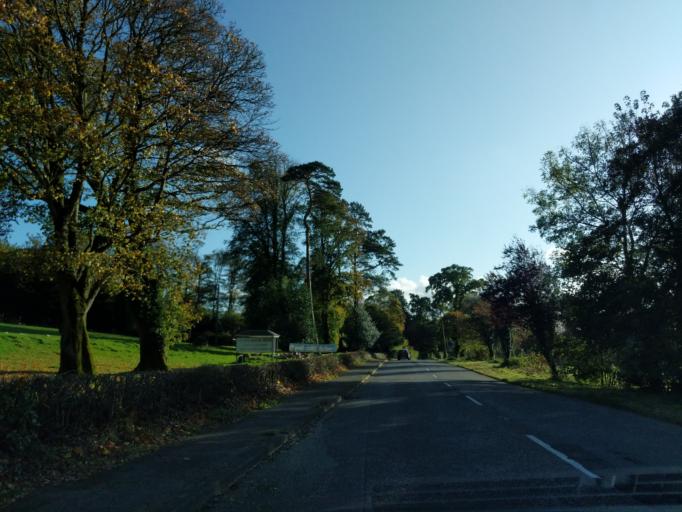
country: GB
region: Scotland
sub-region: Dumfries and Galloway
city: Kirkcudbright
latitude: 54.8523
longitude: -4.0402
